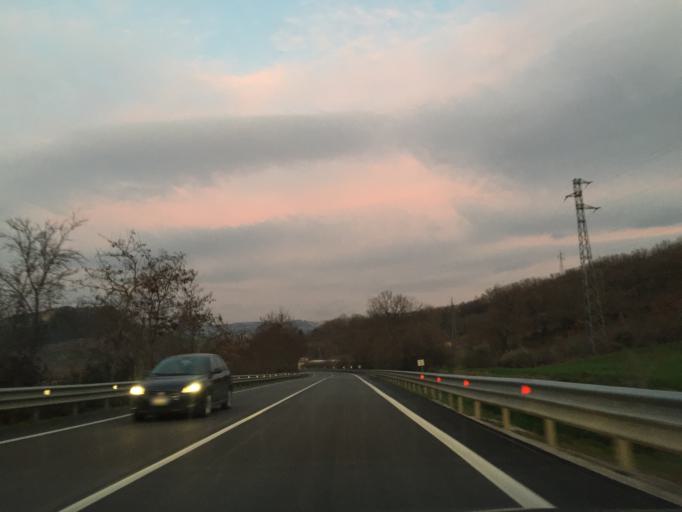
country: IT
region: Molise
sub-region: Provincia di Campobasso
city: Gambatesa
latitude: 41.5237
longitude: 14.9262
